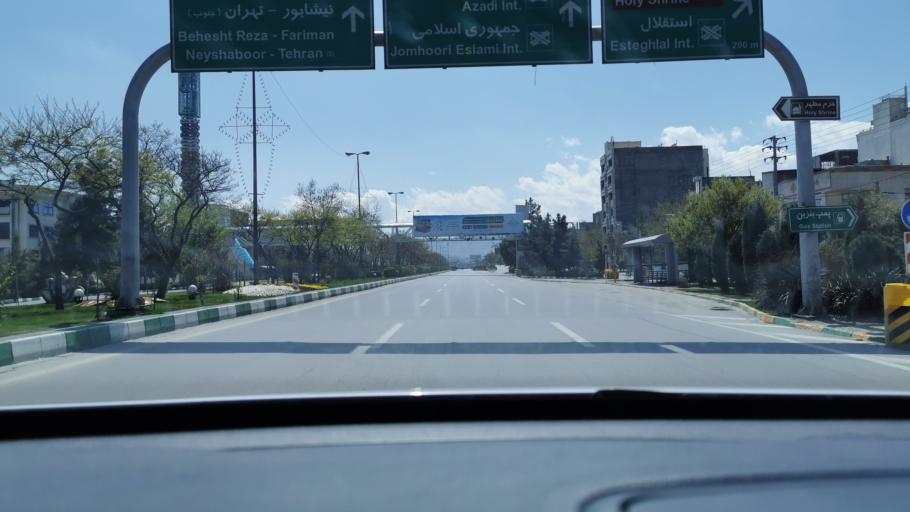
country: IR
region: Razavi Khorasan
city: Mashhad
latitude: 36.3311
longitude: 59.5447
